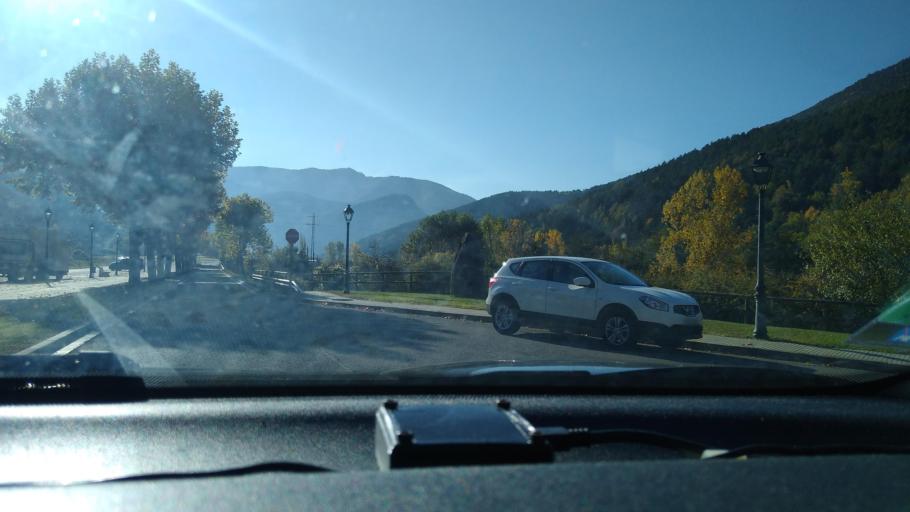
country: ES
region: Catalonia
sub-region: Provincia de Barcelona
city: Baga
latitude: 42.2485
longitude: 1.8667
